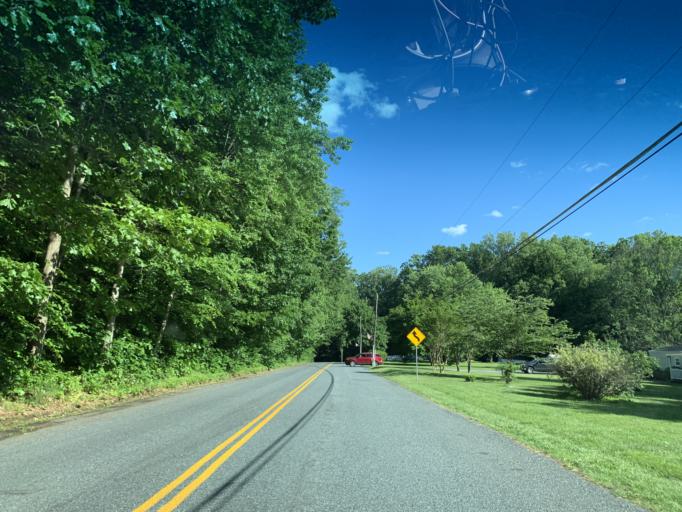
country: US
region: Maryland
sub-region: Harford County
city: South Bel Air
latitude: 39.6438
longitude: -76.2441
